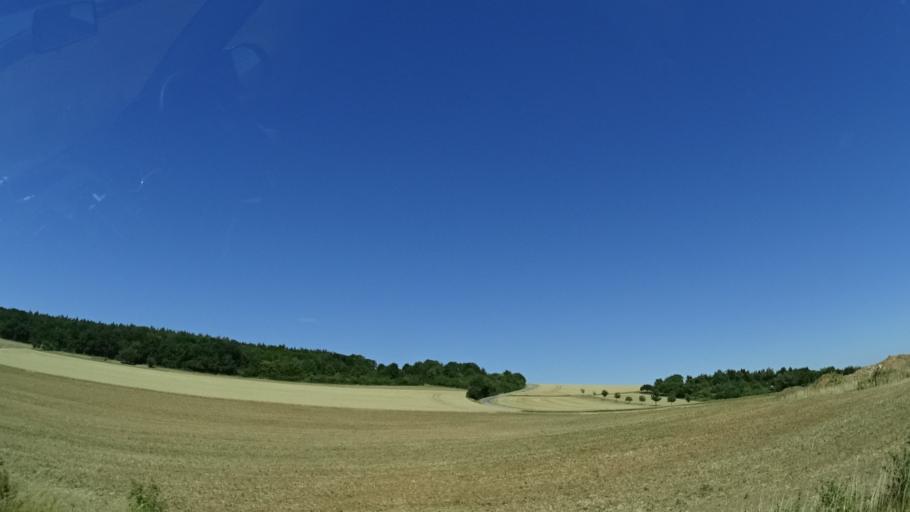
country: DE
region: Bavaria
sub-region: Regierungsbezirk Unterfranken
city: Rimpar
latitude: 49.8636
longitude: 9.9373
